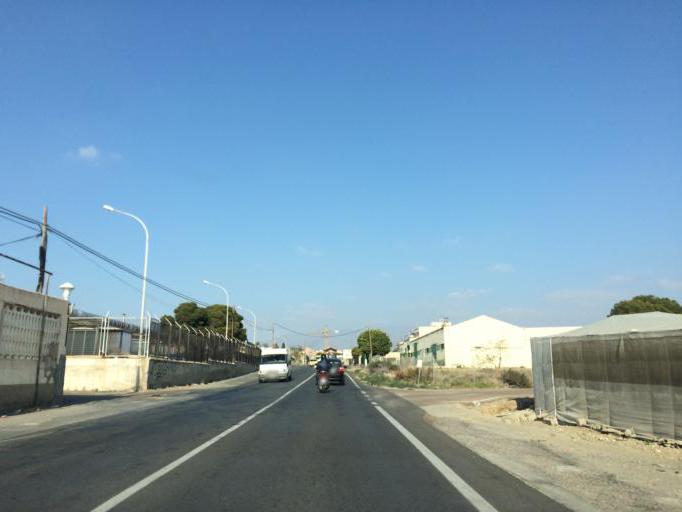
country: ES
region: Andalusia
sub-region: Provincia de Almeria
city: Viator
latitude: 36.8610
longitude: -2.4194
